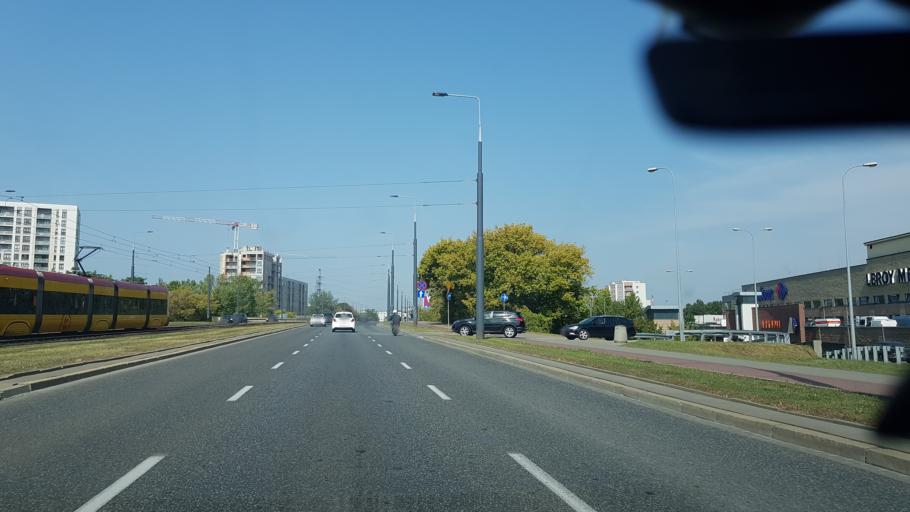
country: PL
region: Masovian Voivodeship
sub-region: Warszawa
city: Zoliborz
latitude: 52.2567
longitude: 20.9819
